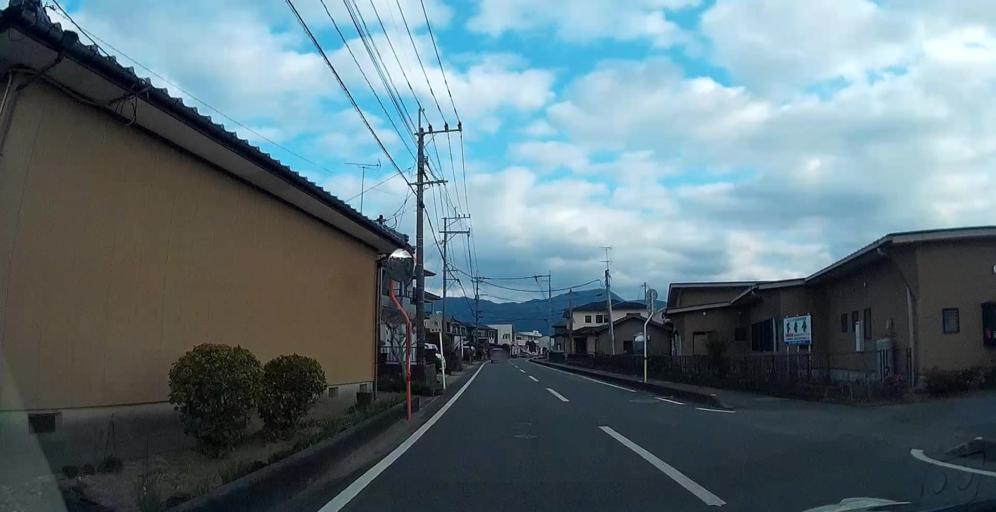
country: JP
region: Kumamoto
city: Yatsushiro
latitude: 32.5387
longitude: 130.6277
